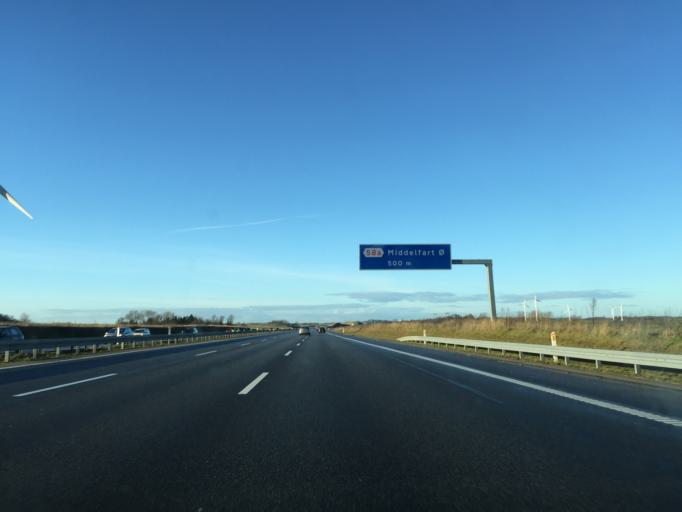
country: DK
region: South Denmark
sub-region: Middelfart Kommune
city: Norre Aby
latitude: 55.4901
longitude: 9.8324
